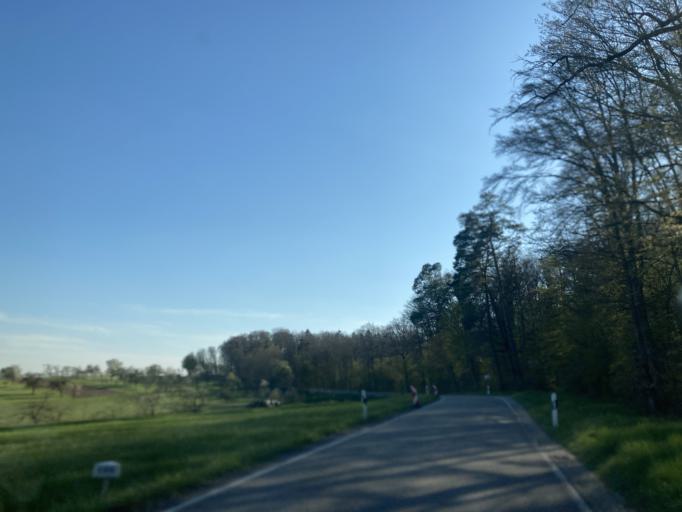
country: DE
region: Baden-Wuerttemberg
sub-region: Regierungsbezirk Stuttgart
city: Hildrizhausen
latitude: 48.5568
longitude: 8.9457
